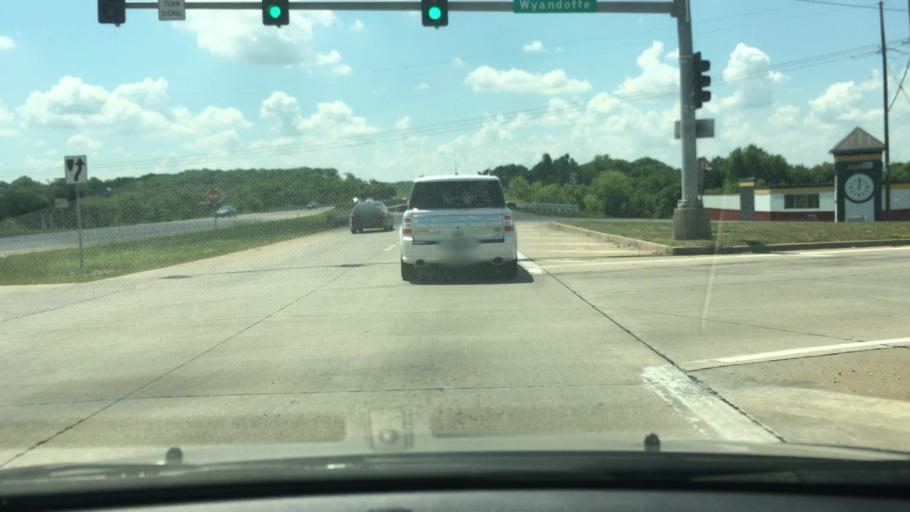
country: US
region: Missouri
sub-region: Jackson County
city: Grandview
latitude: 38.8732
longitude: -94.6031
